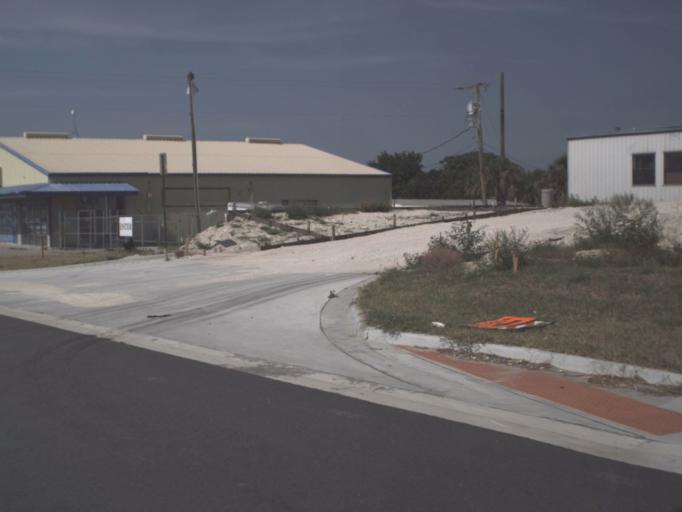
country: US
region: Florida
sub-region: Brevard County
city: Sharpes
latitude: 28.4095
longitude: -80.7551
